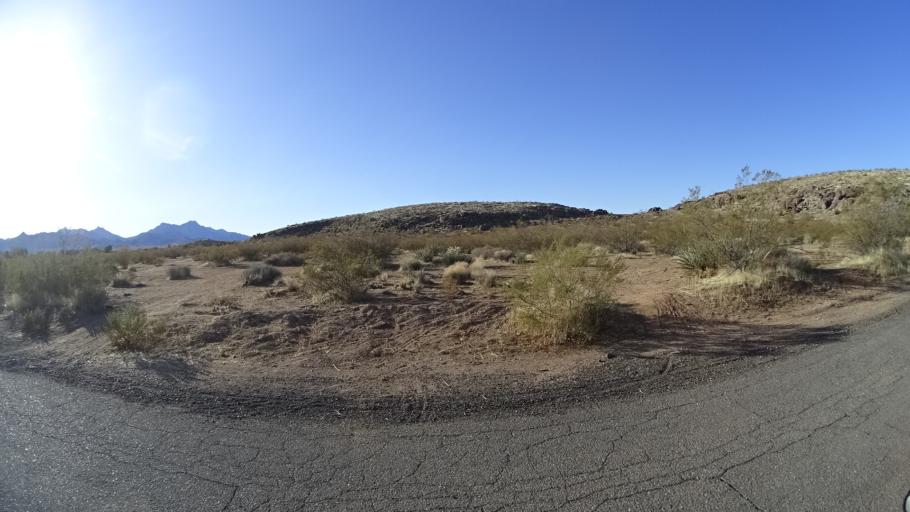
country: US
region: Arizona
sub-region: Mohave County
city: Kingman
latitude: 35.2105
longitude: -114.0050
